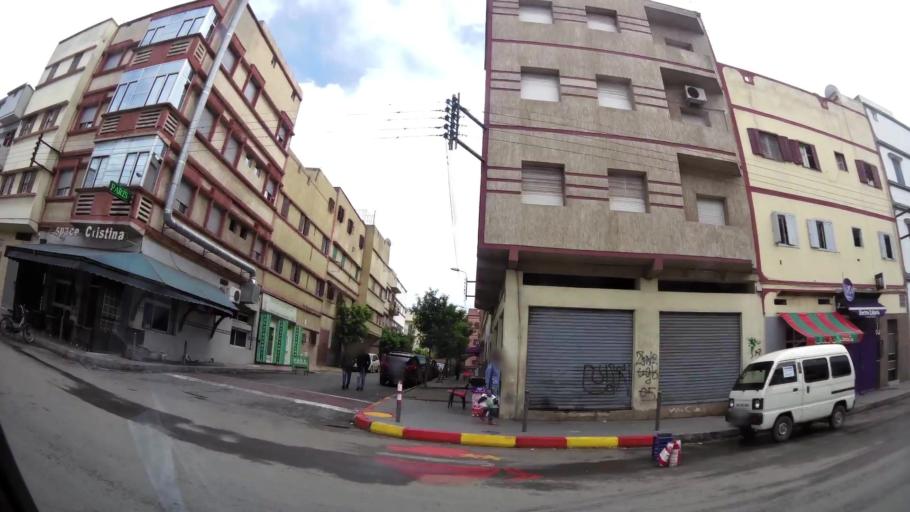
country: MA
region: Grand Casablanca
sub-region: Casablanca
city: Casablanca
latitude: 33.5458
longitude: -7.5650
